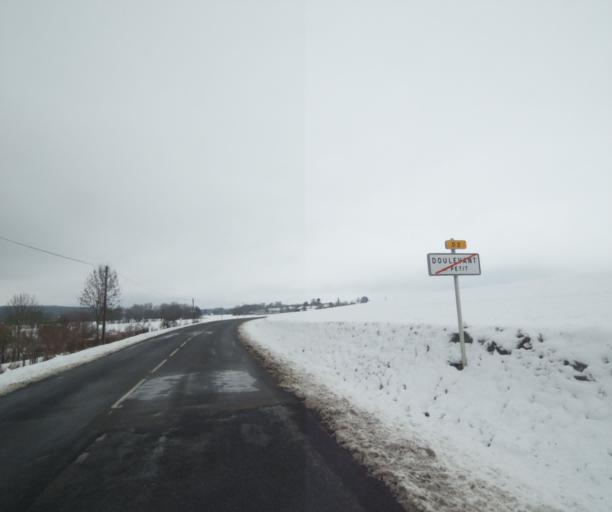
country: FR
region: Champagne-Ardenne
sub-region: Departement de la Haute-Marne
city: Wassy
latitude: 48.4485
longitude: 4.9574
